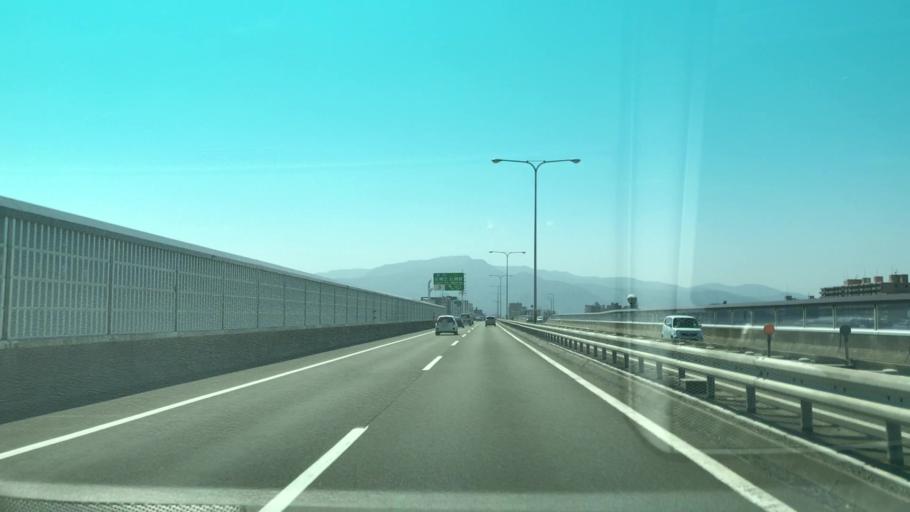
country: JP
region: Hokkaido
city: Sapporo
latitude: 43.1038
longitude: 141.3607
